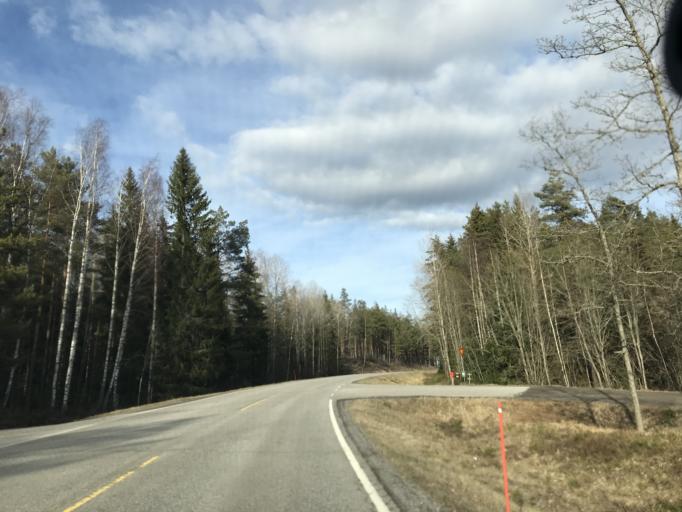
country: FI
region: Uusimaa
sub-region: Raaseporin
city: Ekenaes
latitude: 60.0794
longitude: 23.3531
